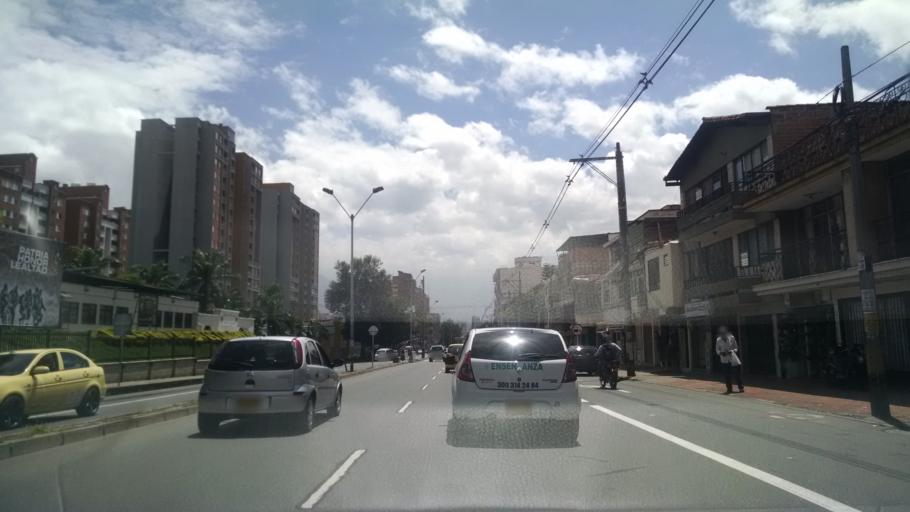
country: CO
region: Antioquia
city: Medellin
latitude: 6.2613
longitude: -75.5921
